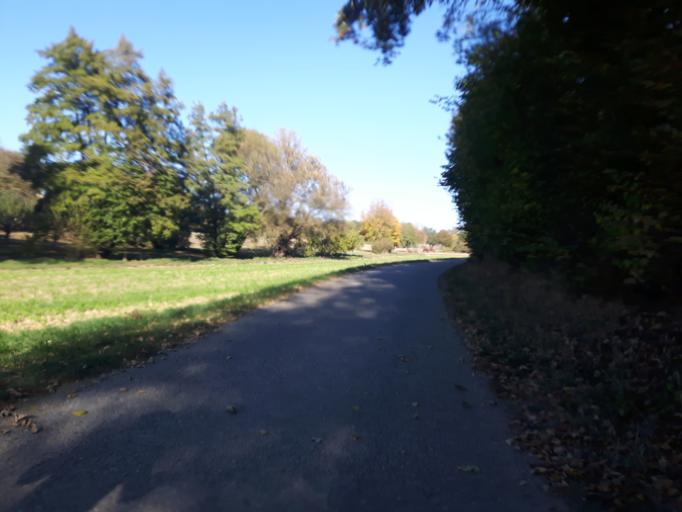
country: DE
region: Baden-Wuerttemberg
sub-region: Regierungsbezirk Stuttgart
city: Bad Wimpfen
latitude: 49.2024
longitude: 9.1389
